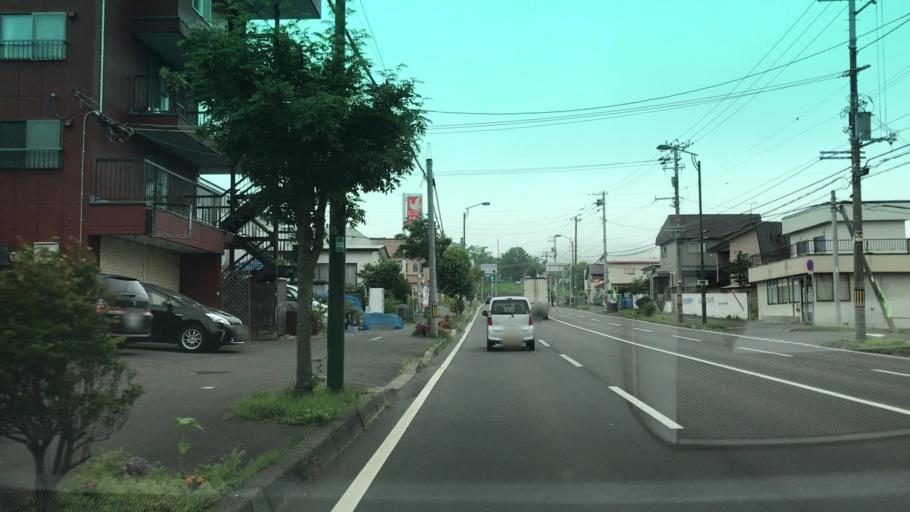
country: JP
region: Hokkaido
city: Muroran
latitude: 42.3639
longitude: 141.0380
